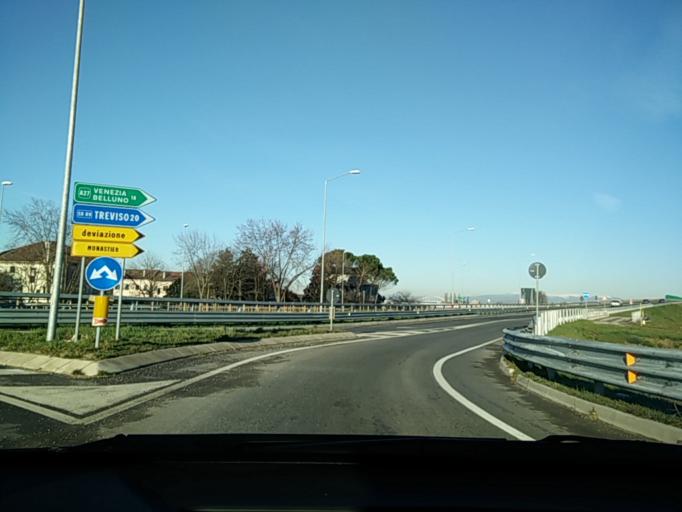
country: IT
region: Veneto
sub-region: Provincia di Venezia
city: Meolo
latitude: 45.6287
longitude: 12.4496
